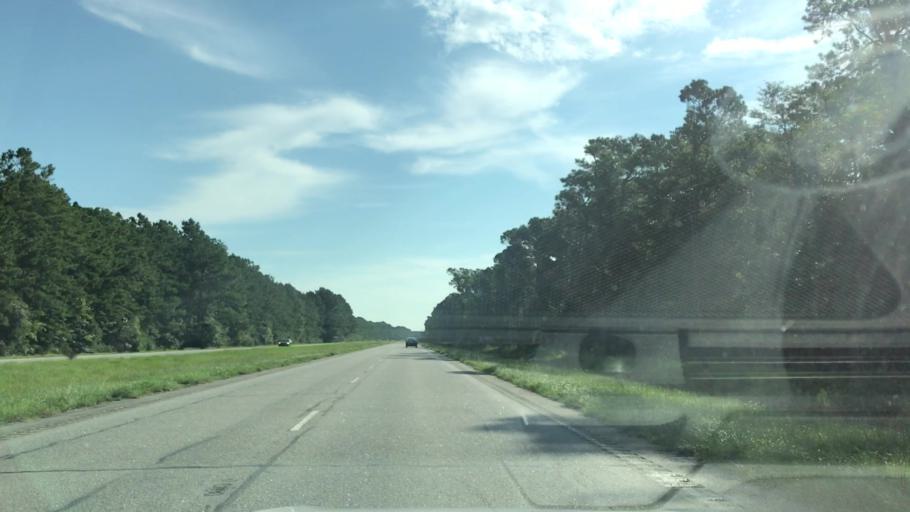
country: US
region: South Carolina
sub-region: Charleston County
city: Awendaw
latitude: 33.0656
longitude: -79.5298
